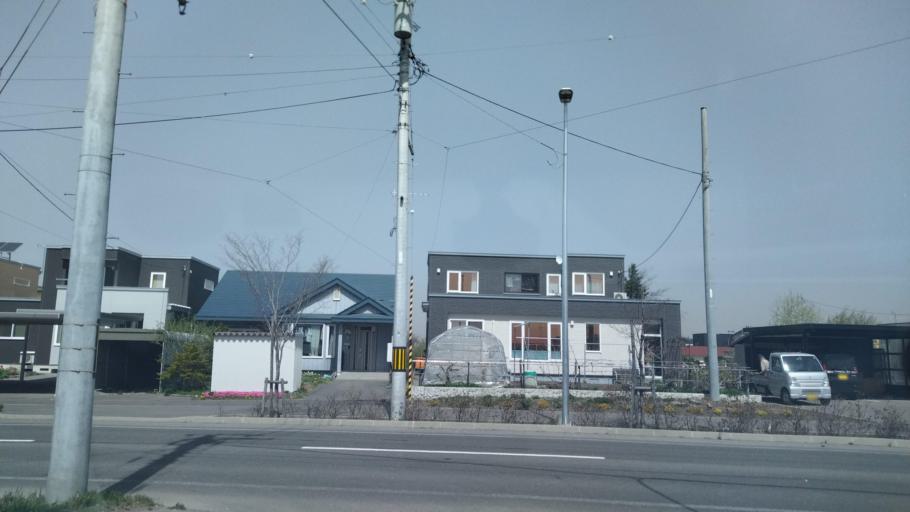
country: JP
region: Hokkaido
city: Obihiro
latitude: 42.9358
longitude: 143.1879
